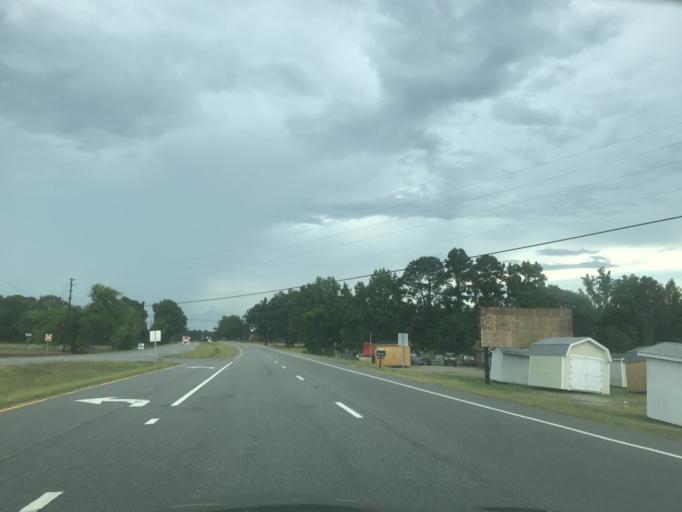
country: US
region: North Carolina
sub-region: Johnston County
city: Wilsons Mills
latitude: 35.5631
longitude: -78.3918
